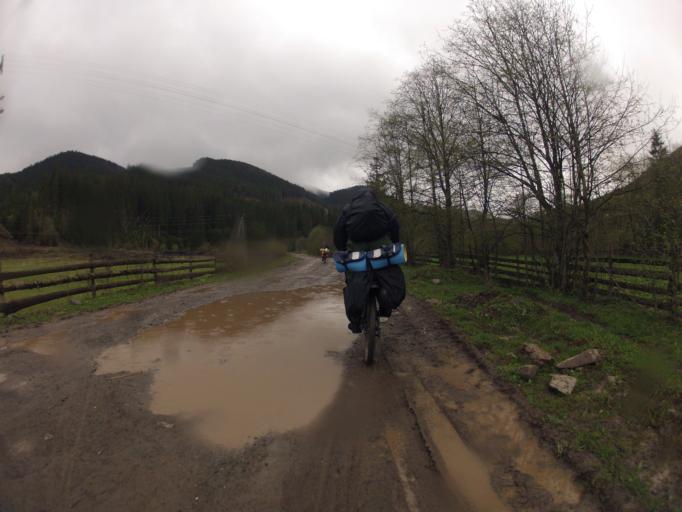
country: RO
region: Suceava
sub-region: Comuna Izvoarele Sucevei
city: Izvoarele Sucevei
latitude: 47.8336
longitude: 25.0535
